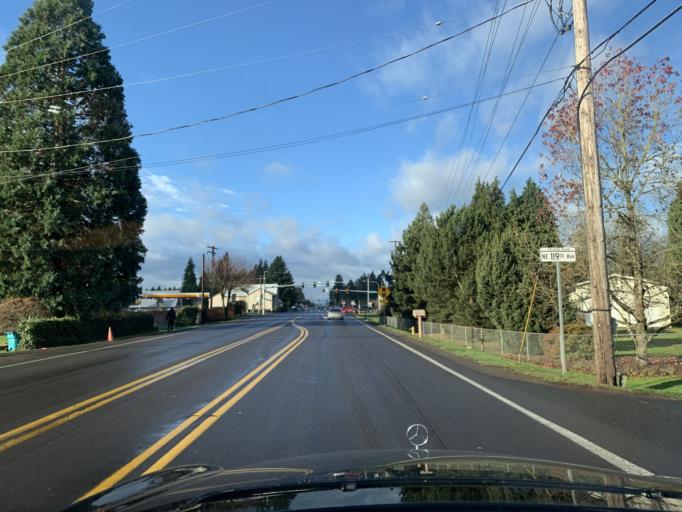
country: US
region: Washington
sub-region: Clark County
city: Brush Prairie
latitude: 45.7080
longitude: -122.5507
